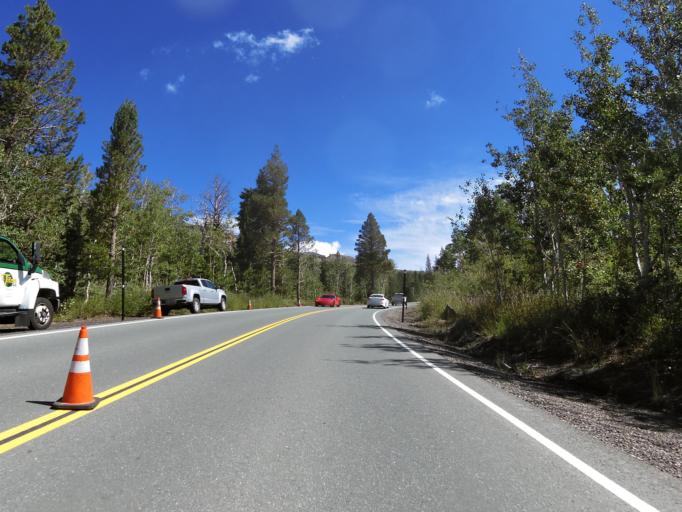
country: US
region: California
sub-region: El Dorado County
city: South Lake Tahoe
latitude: 38.6999
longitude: -120.0248
